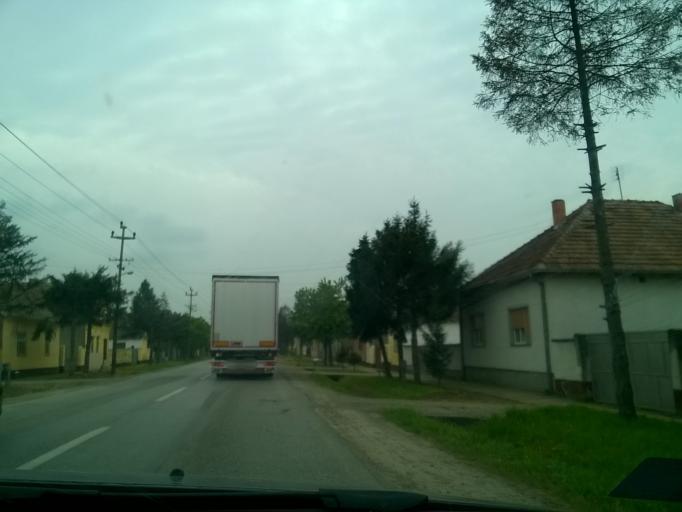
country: RS
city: Hrtkovci
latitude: 44.8804
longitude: 19.7655
